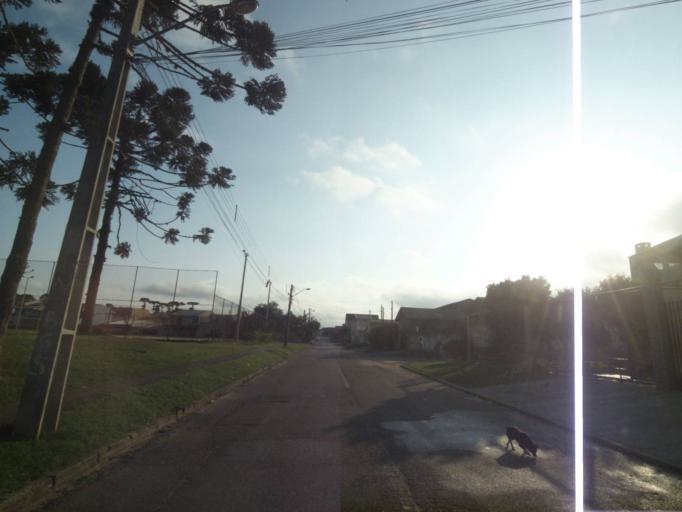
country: BR
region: Parana
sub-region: Sao Jose Dos Pinhais
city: Sao Jose dos Pinhais
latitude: -25.5443
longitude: -49.2478
